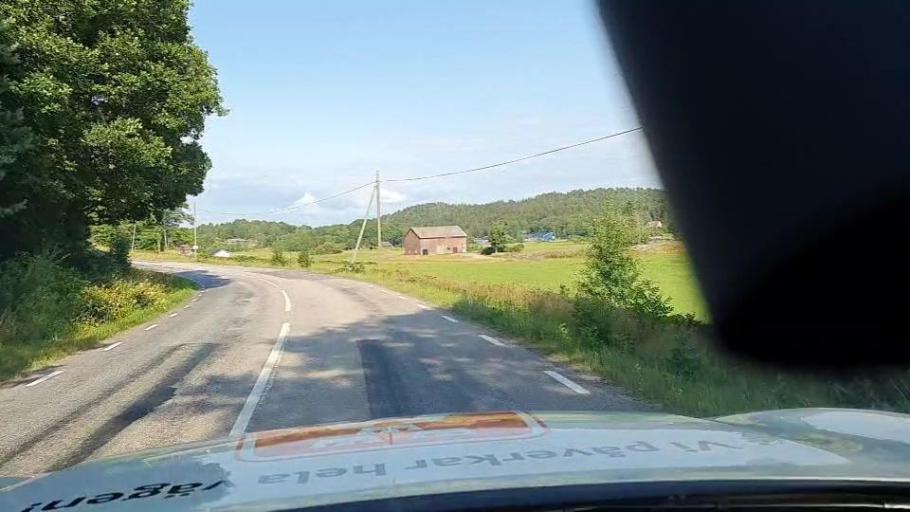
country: SE
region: Vaestra Goetaland
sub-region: Orust
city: Henan
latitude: 58.2260
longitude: 11.6313
